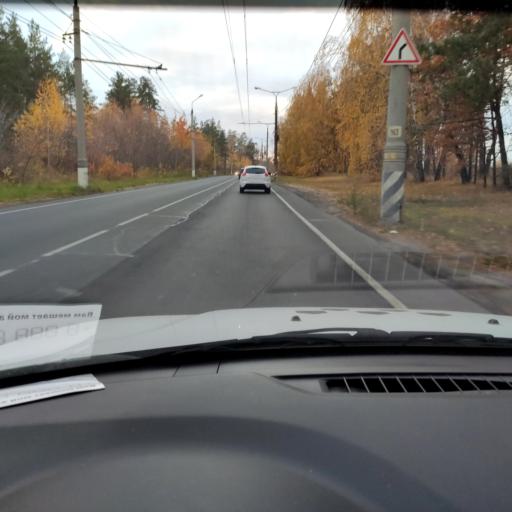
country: RU
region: Samara
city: Tol'yatti
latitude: 53.4919
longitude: 49.3857
